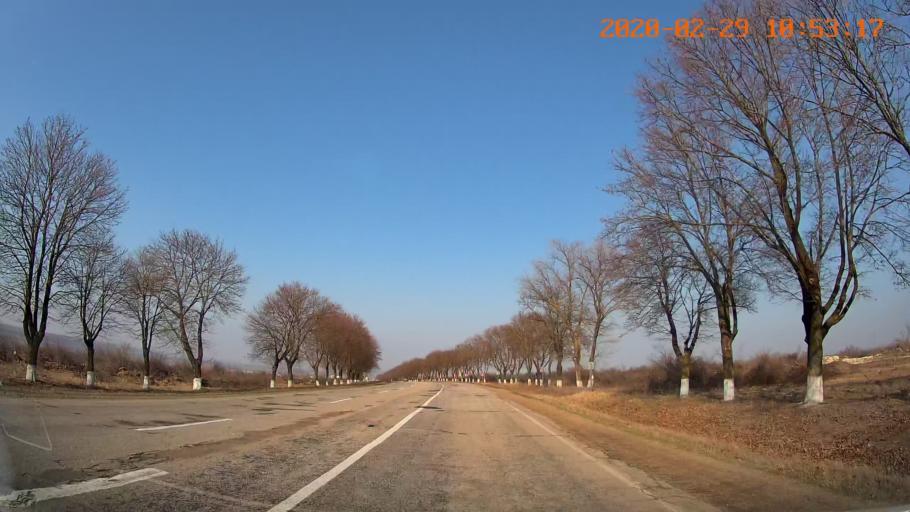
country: MD
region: Telenesti
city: Grigoriopol
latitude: 47.1144
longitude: 29.3382
